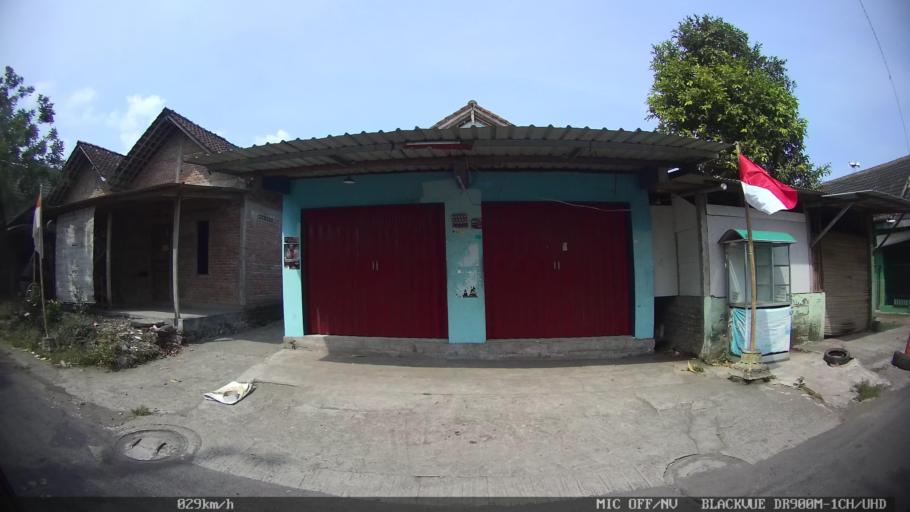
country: ID
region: Daerah Istimewa Yogyakarta
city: Depok
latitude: -7.8018
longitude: 110.4452
